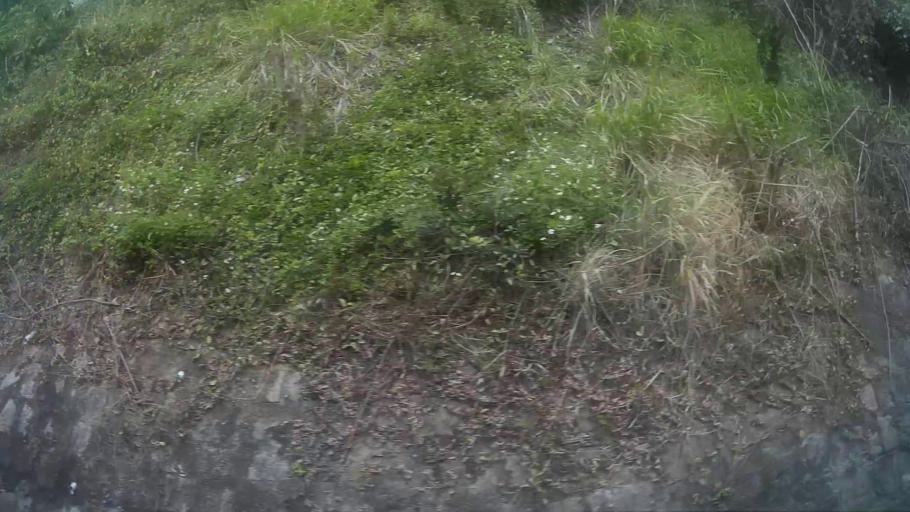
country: VN
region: Khanh Hoa
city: Van Gia
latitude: 12.8534
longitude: 109.3953
